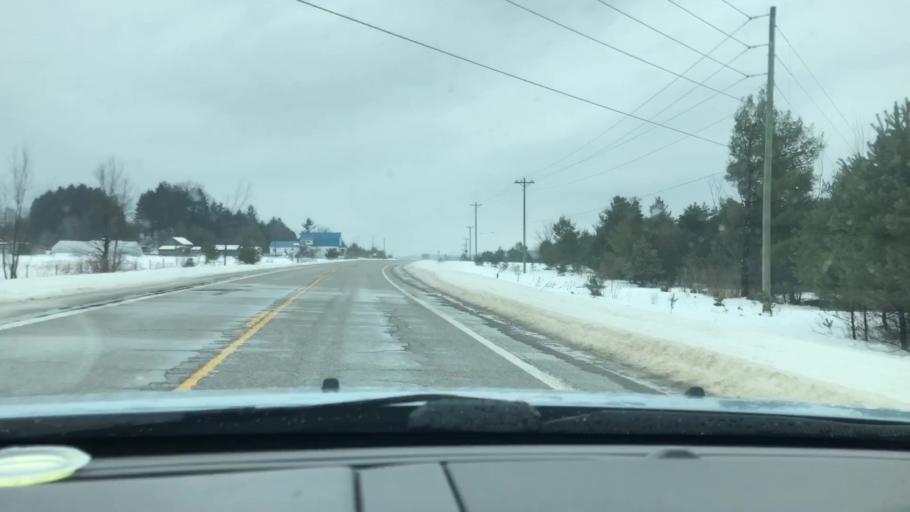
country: US
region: Michigan
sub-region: Charlevoix County
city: East Jordan
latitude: 45.1133
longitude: -85.1293
